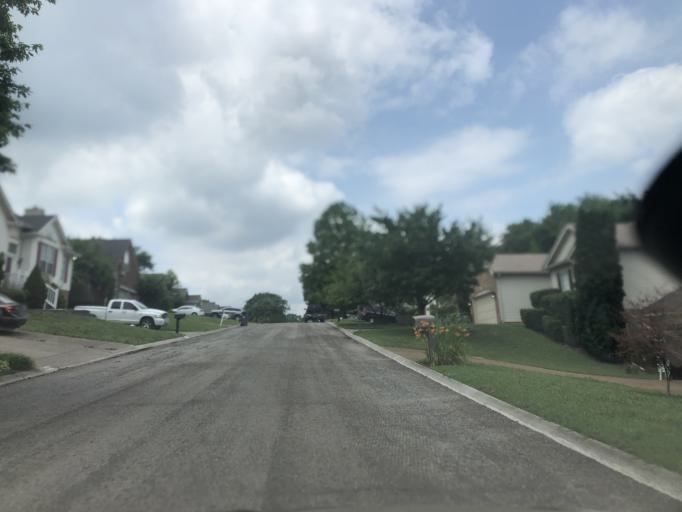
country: US
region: Tennessee
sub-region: Davidson County
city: Lakewood
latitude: 36.2180
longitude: -86.6303
